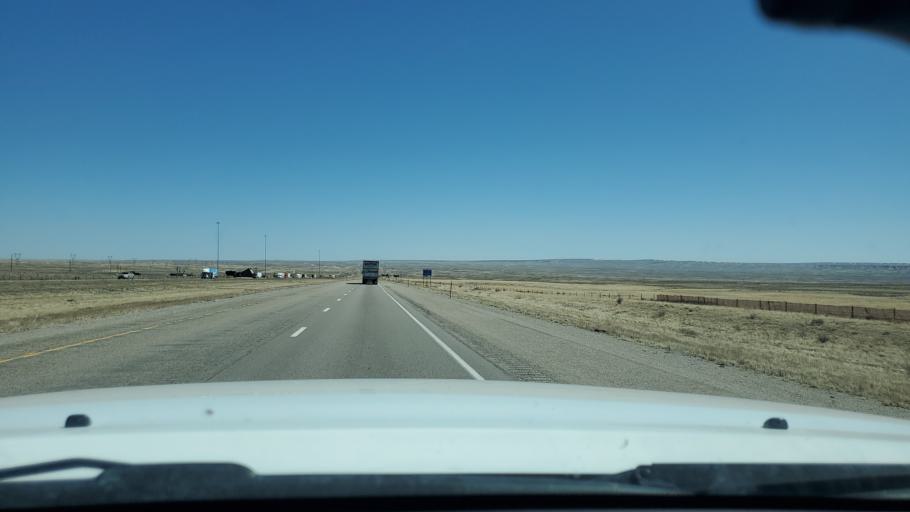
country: US
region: Wyoming
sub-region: Sweetwater County
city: Rock Springs
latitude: 41.6438
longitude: -108.5543
